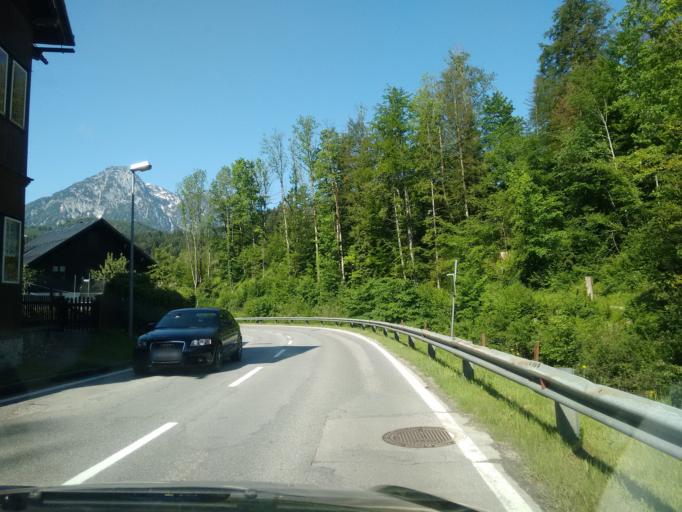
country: AT
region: Styria
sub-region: Politischer Bezirk Liezen
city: Altaussee
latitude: 47.6304
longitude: 13.7637
